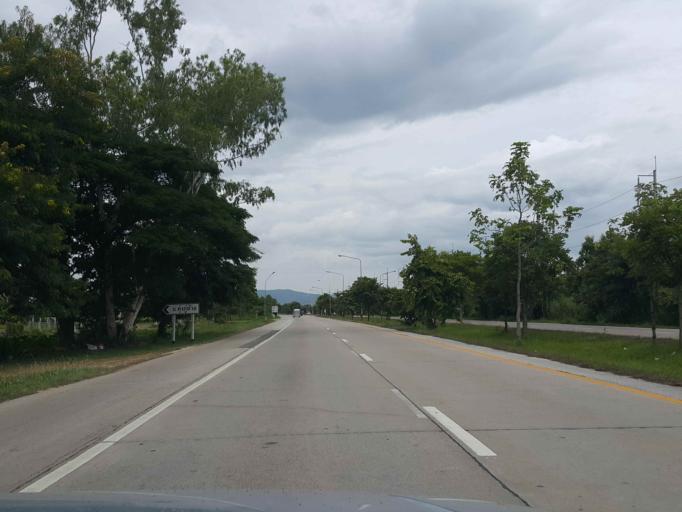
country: TH
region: Lampang
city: Lampang
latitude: 18.2919
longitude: 99.4262
